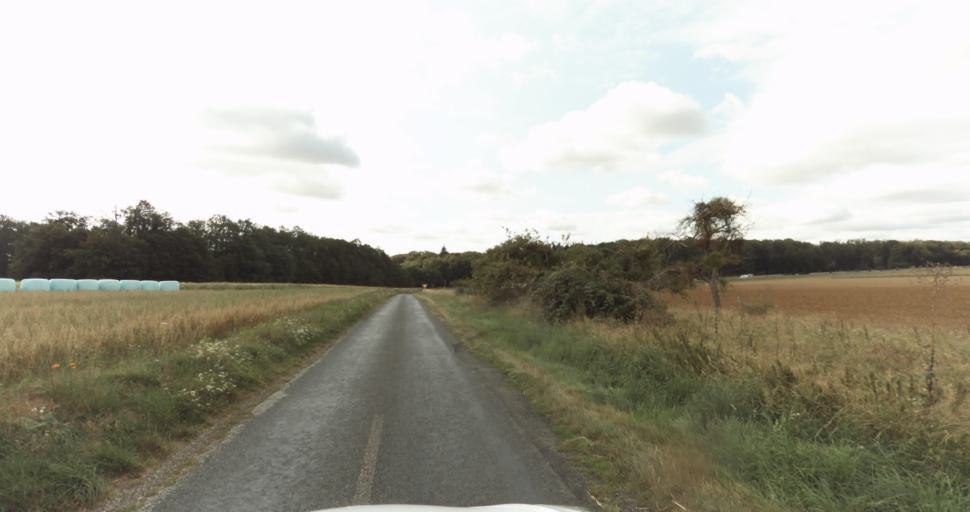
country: FR
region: Haute-Normandie
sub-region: Departement de l'Eure
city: Tillieres-sur-Avre
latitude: 48.7767
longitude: 1.1053
